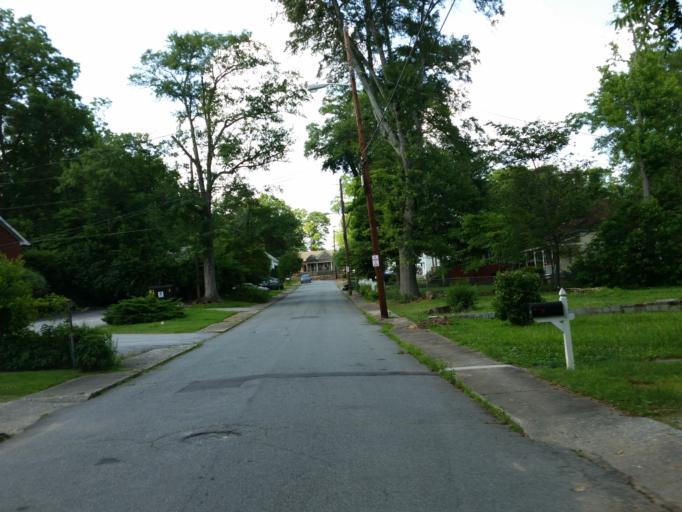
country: US
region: Georgia
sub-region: Cobb County
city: Marietta
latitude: 33.9402
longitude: -84.5412
